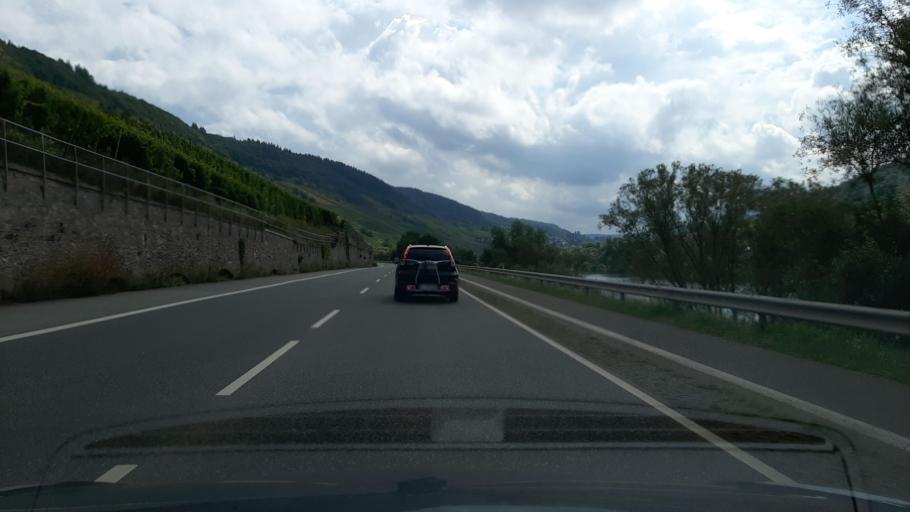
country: DE
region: Rheinland-Pfalz
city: Reil
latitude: 50.0221
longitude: 7.1202
